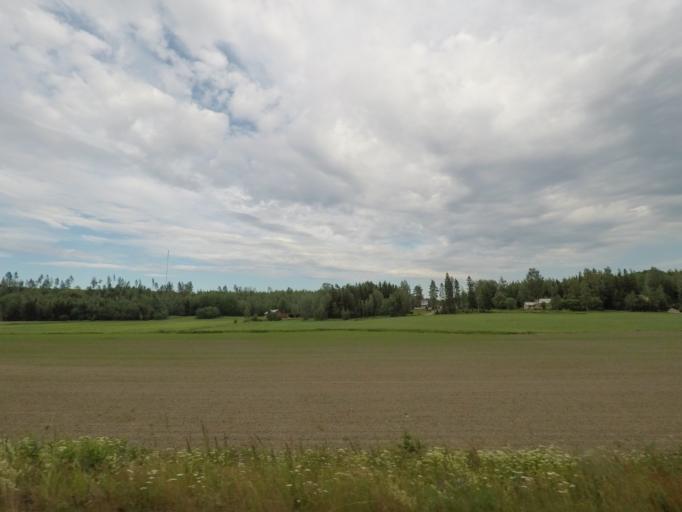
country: FI
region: Uusimaa
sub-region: Porvoo
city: Pukkila
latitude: 60.7785
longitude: 25.4555
